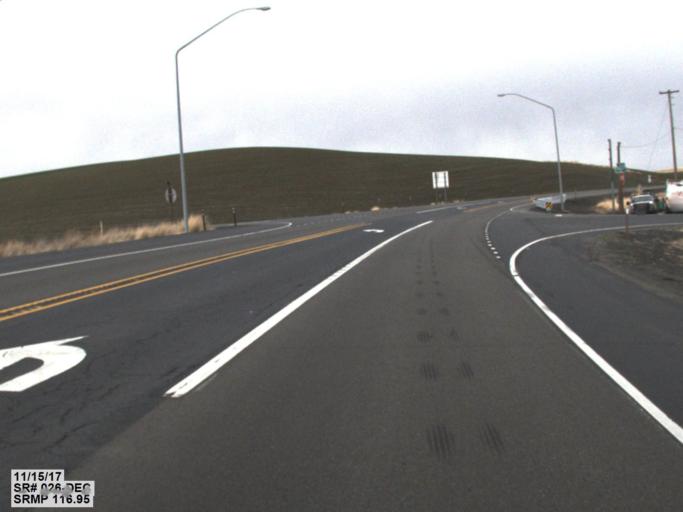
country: US
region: Washington
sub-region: Whitman County
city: Colfax
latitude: 46.8090
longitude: -117.6544
